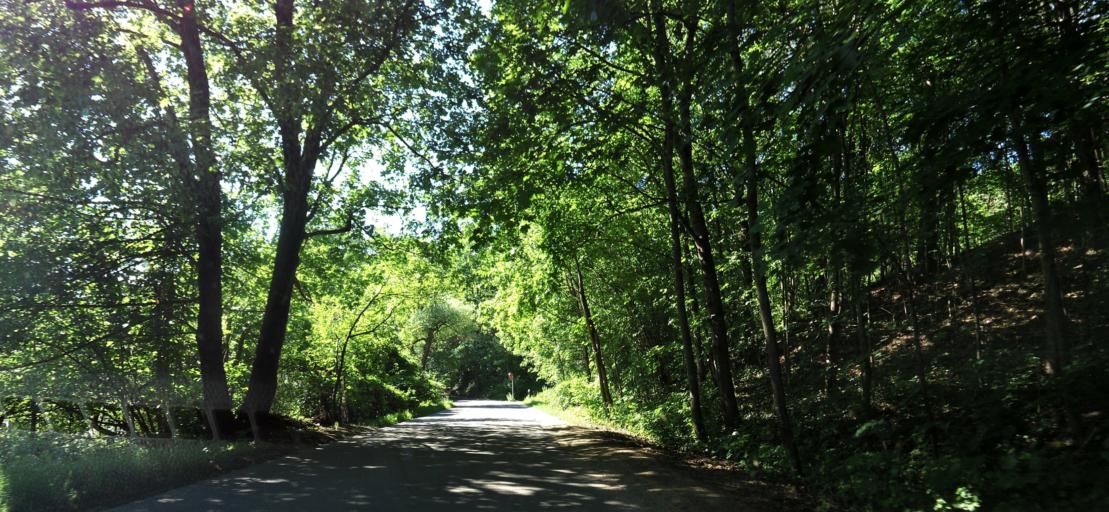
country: LT
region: Vilnius County
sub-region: Vilnius
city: Fabijoniskes
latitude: 54.7487
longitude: 25.3018
